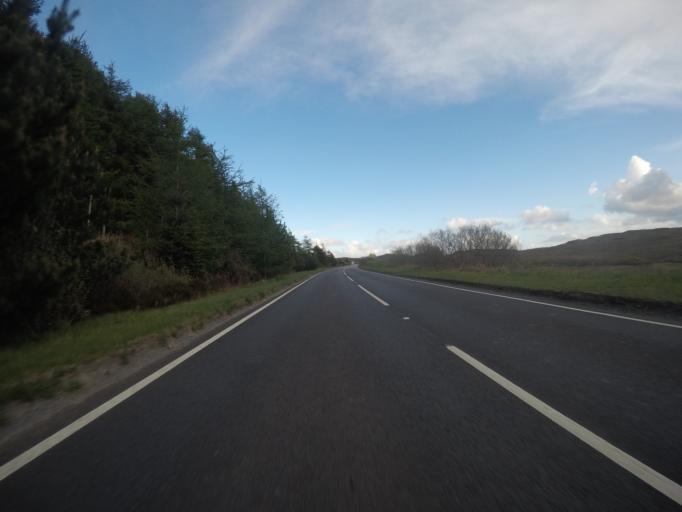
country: GB
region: Scotland
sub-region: Highland
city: Portree
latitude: 57.5262
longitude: -6.3461
